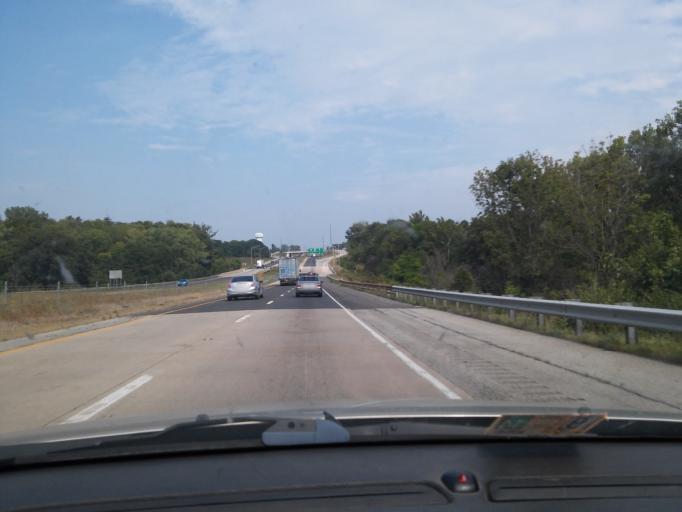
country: US
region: Indiana
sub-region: Wayne County
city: Richmond
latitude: 39.8709
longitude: -84.9001
